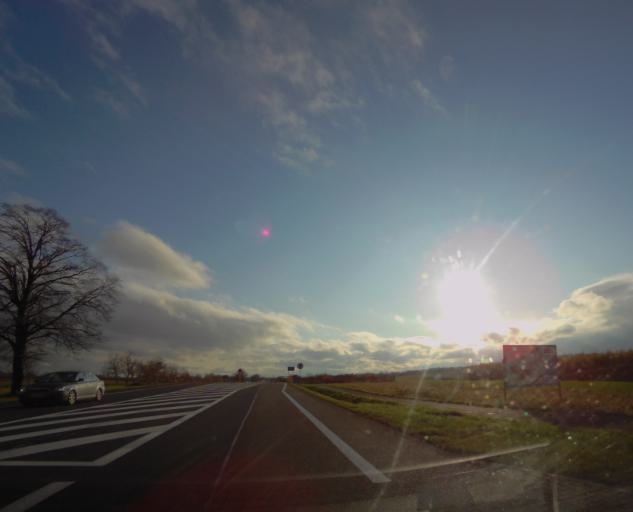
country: PL
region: Subcarpathian Voivodeship
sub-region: Powiat przemyski
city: Orly
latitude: 49.8523
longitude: 22.8047
